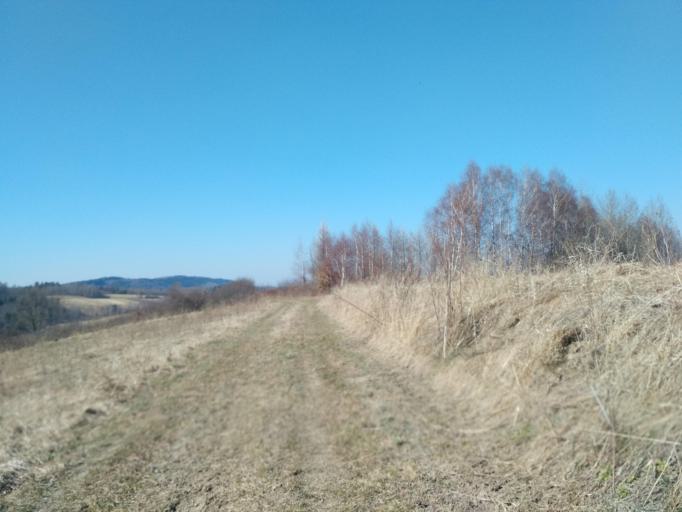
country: PL
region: Subcarpathian Voivodeship
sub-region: Powiat brzozowski
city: Golcowa
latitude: 49.7642
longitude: 22.0290
